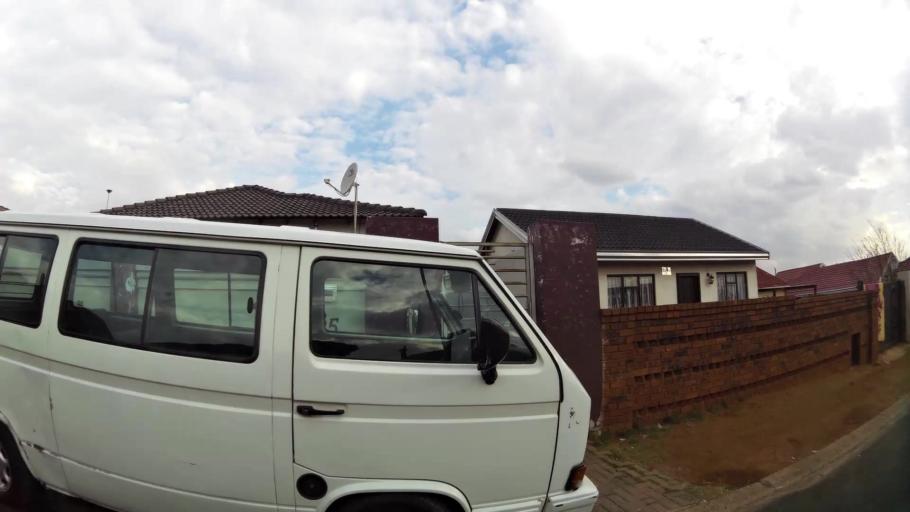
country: ZA
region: Gauteng
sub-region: City of Johannesburg Metropolitan Municipality
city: Soweto
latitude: -26.2441
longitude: 27.8116
